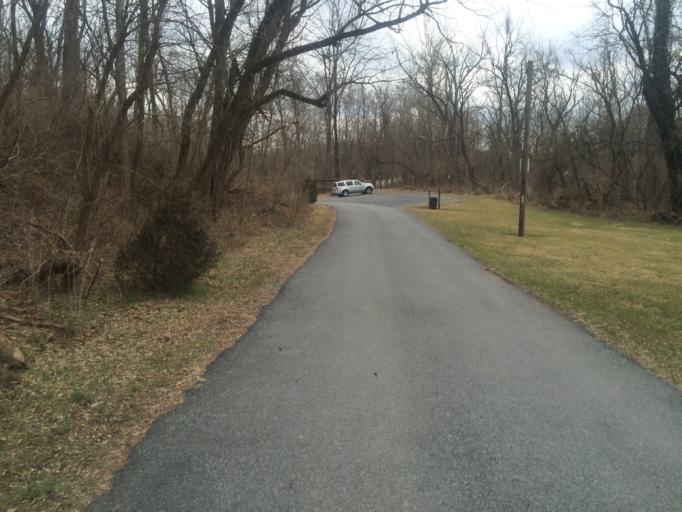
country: US
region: Pennsylvania
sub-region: Lebanon County
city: Annville
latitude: 40.3280
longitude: -76.5074
